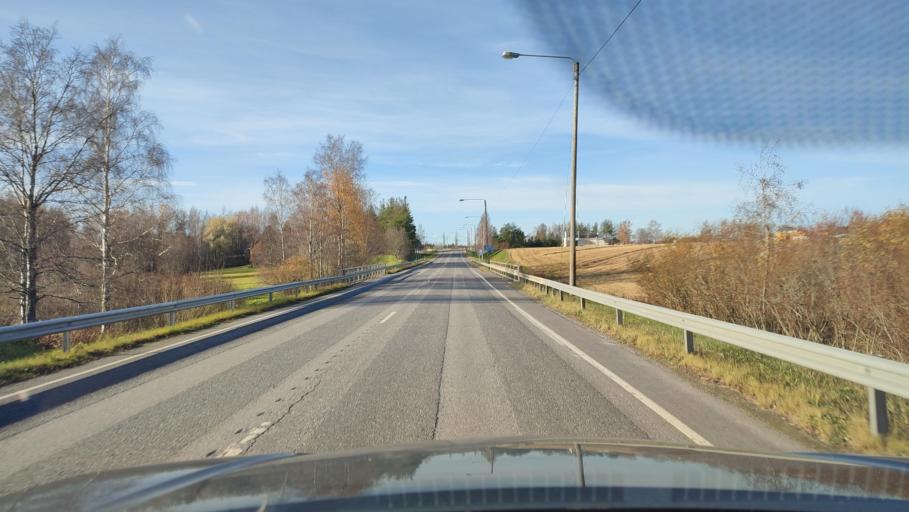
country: FI
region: Southern Ostrobothnia
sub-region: Suupohja
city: Teuva
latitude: 62.4915
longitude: 21.7564
